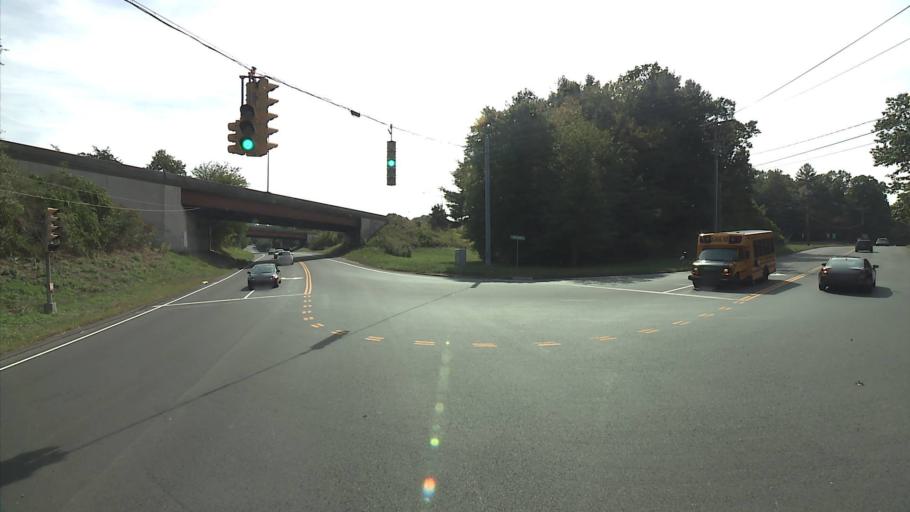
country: US
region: Connecticut
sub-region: Fairfield County
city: Newtown
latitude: 41.4098
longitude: -73.2679
